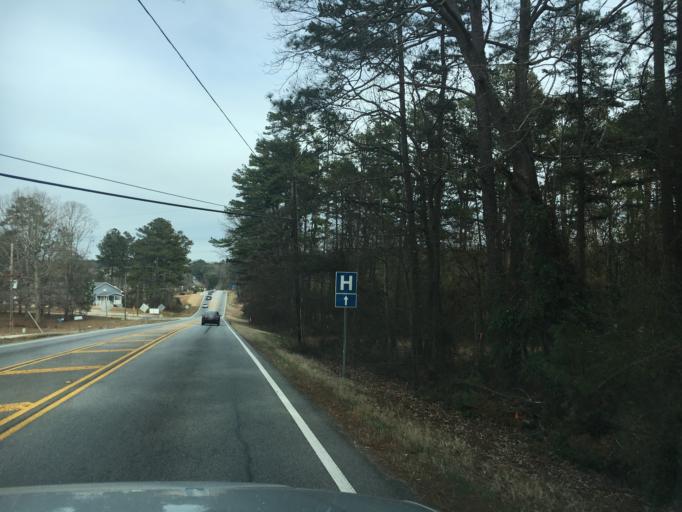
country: US
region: Georgia
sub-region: Barrow County
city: Winder
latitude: 33.9714
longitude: -83.7432
